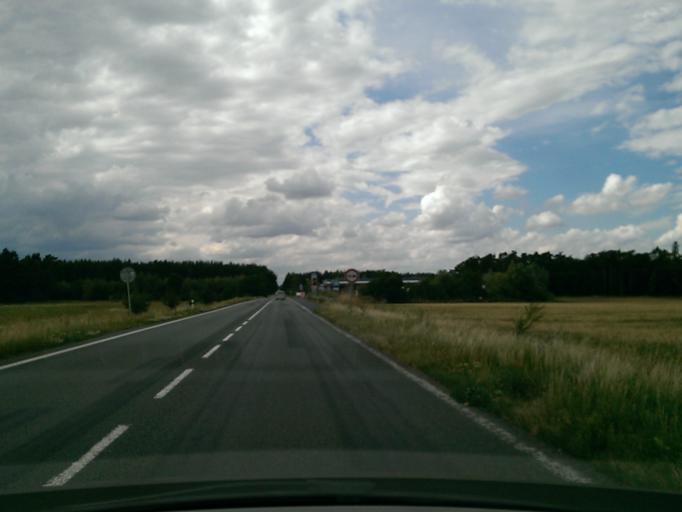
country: CZ
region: Central Bohemia
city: Libice nad Cidlinou
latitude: 50.1056
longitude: 15.1409
